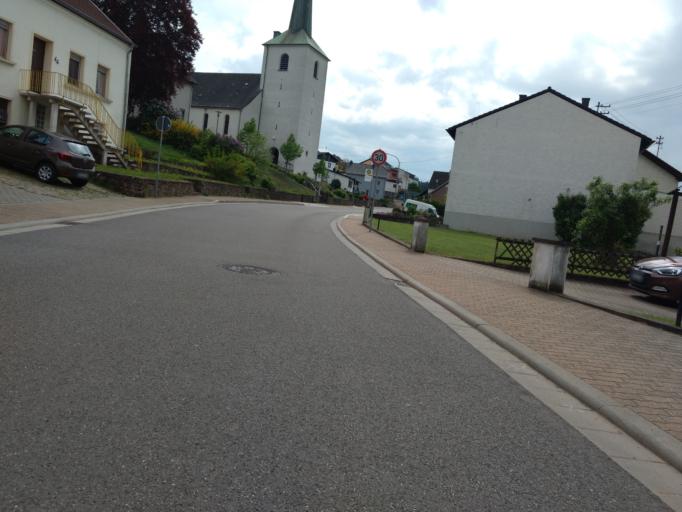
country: DE
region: Saarland
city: Saarwellingen
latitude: 49.3847
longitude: 6.8229
